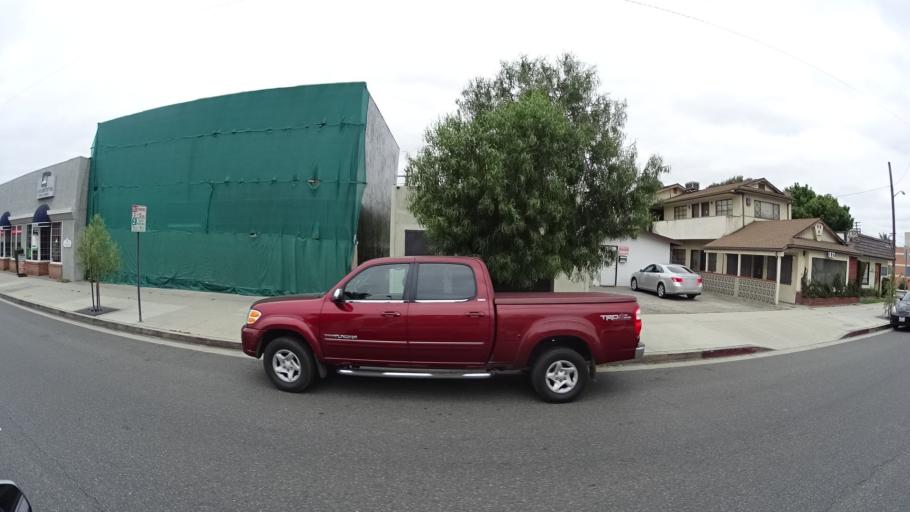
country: US
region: California
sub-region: Los Angeles County
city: Burbank
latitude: 34.1808
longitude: -118.3317
